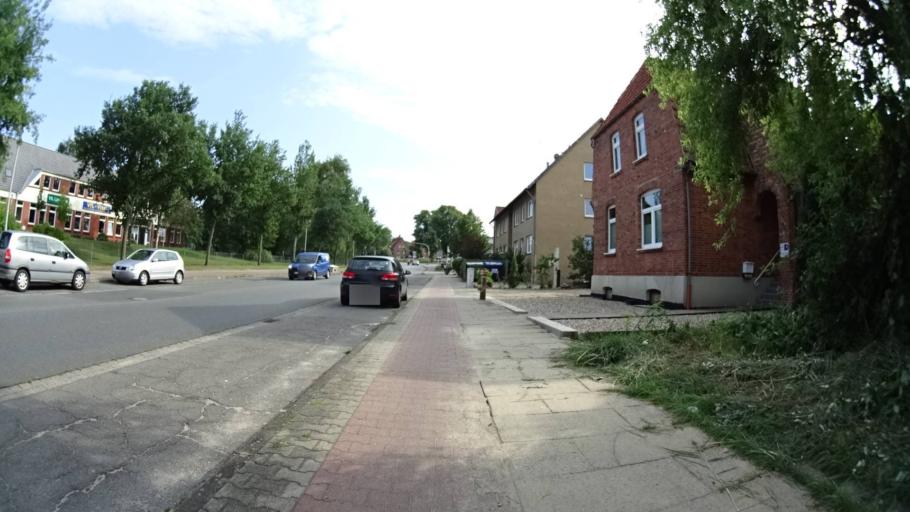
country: DE
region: Lower Saxony
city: Lueneburg
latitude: 53.2457
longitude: 10.3912
